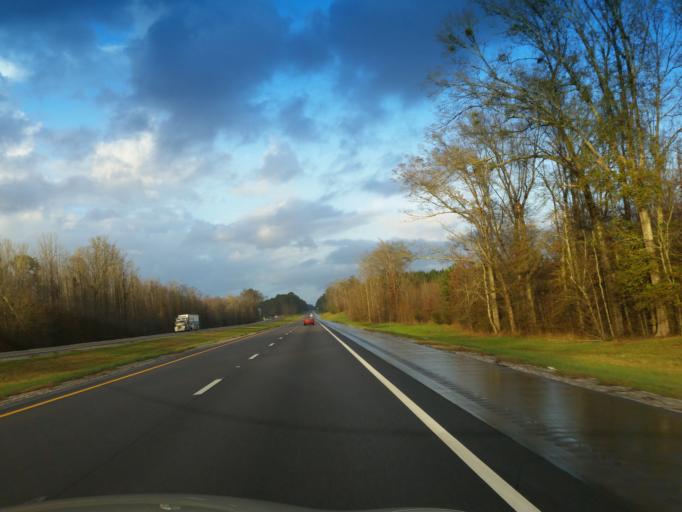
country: US
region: Mississippi
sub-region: Jones County
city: Sharon
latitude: 31.9393
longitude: -88.9903
